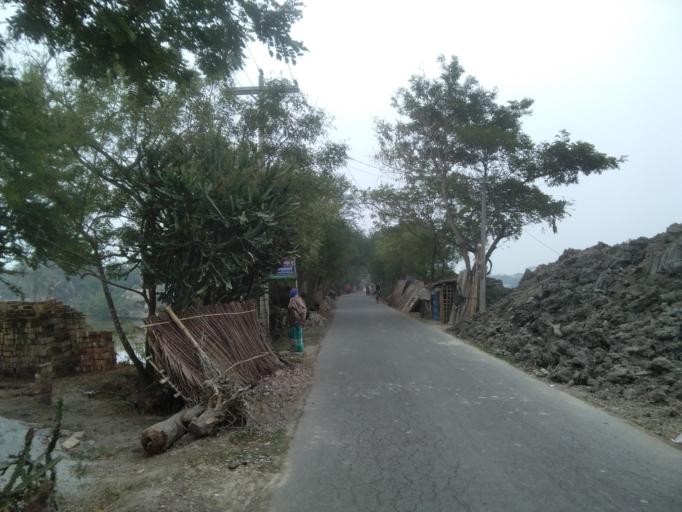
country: BD
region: Khulna
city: Satkhira
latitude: 22.5858
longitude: 89.0660
